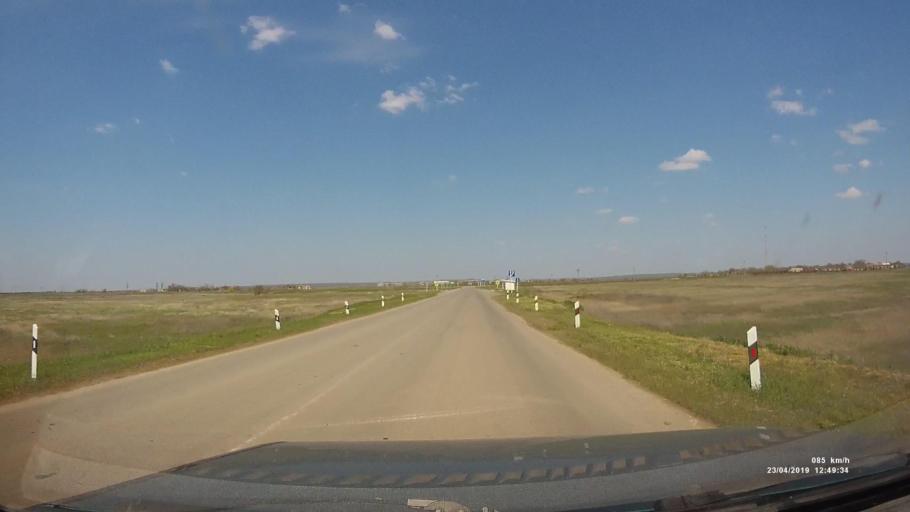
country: RU
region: Kalmykiya
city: Yashalta
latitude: 46.5388
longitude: 42.6399
